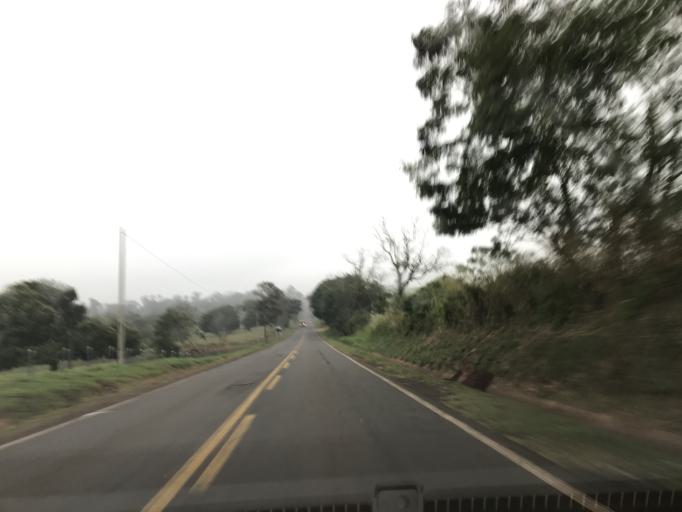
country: PY
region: Canindeyu
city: Salto del Guaira
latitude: -24.0960
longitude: -54.0984
